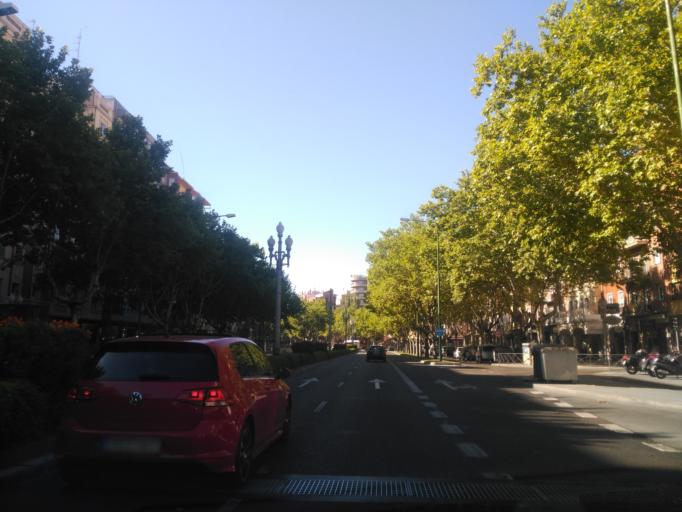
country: ES
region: Castille and Leon
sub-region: Provincia de Valladolid
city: Valladolid
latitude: 41.6438
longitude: -4.7354
